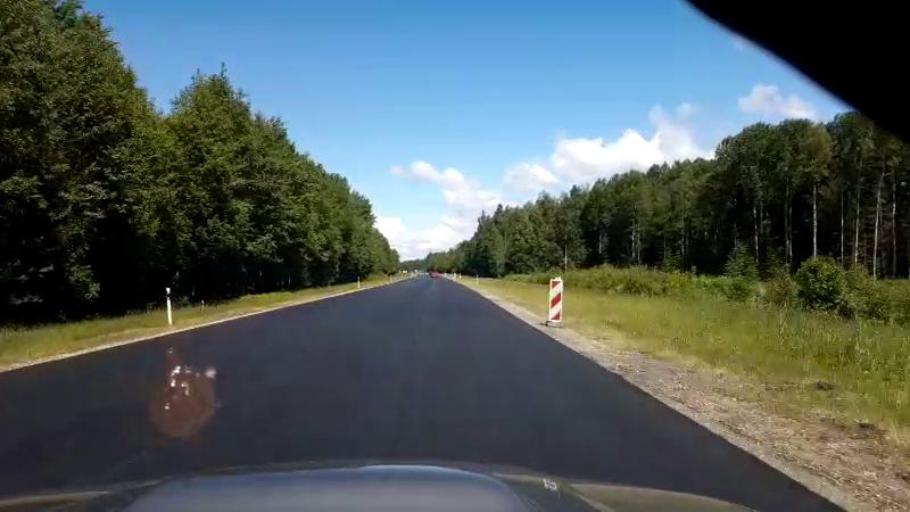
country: LV
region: Salacgrivas
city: Ainazi
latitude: 58.0258
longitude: 24.5022
